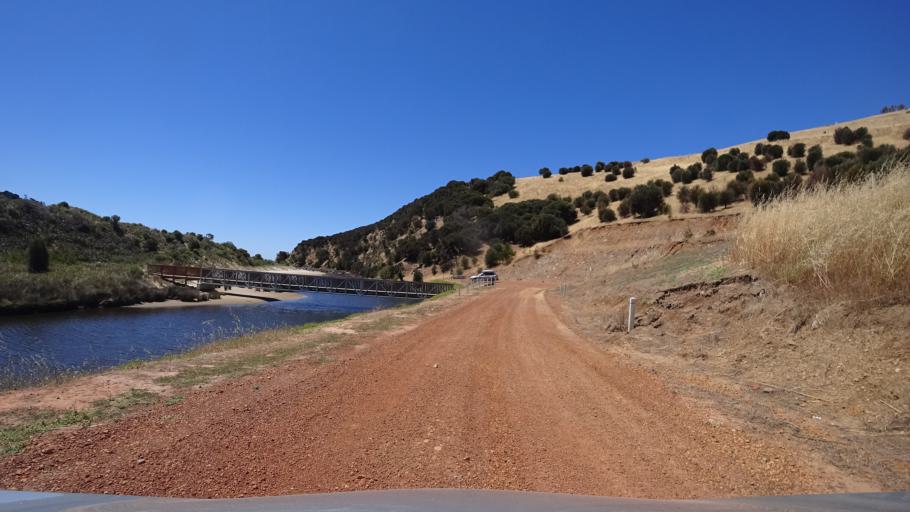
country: AU
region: South Australia
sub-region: Kangaroo Island
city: Kingscote
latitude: -35.6778
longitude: 136.9712
